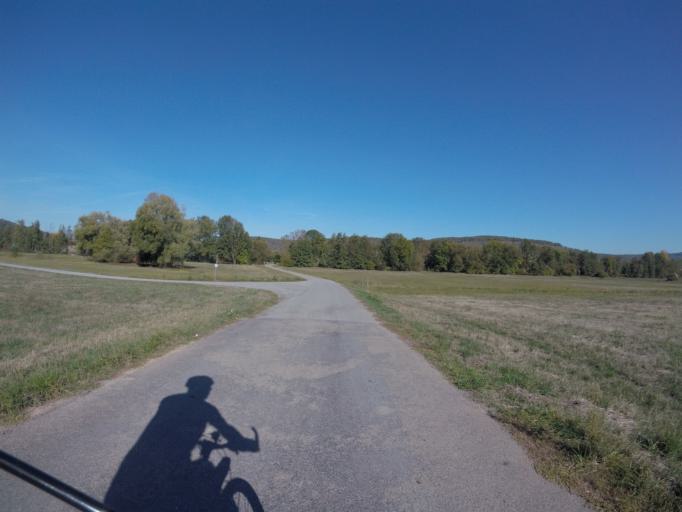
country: DE
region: Baden-Wuerttemberg
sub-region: Karlsruhe Region
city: Illingen
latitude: 48.9895
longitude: 8.9320
